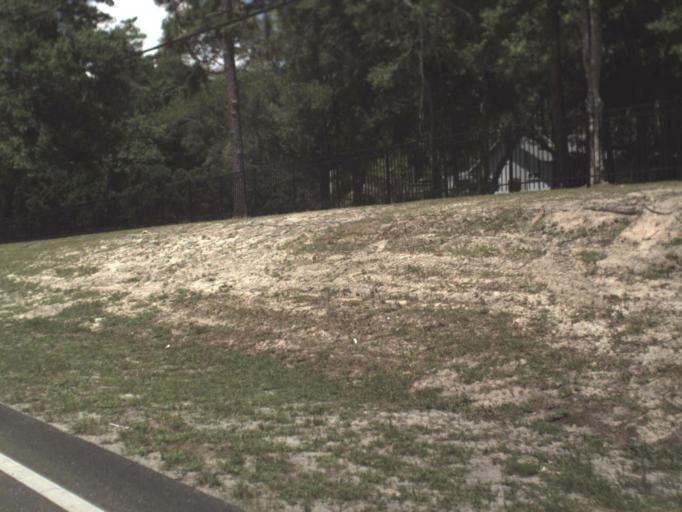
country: US
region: Florida
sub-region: Clay County
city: Keystone Heights
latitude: 29.7648
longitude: -82.0537
